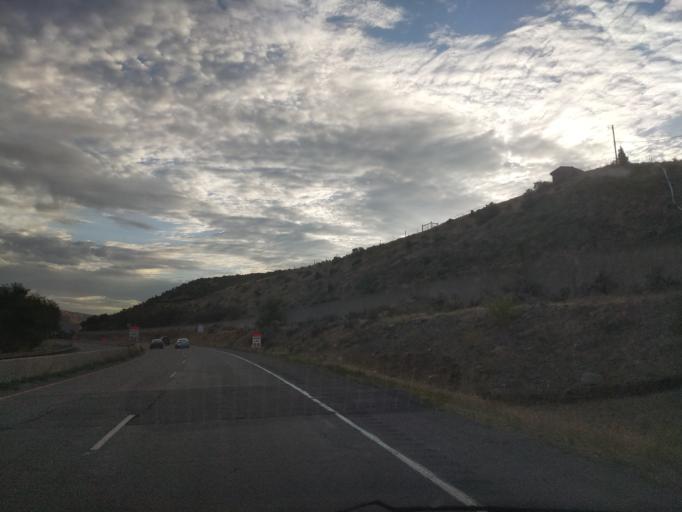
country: US
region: Colorado
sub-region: Mesa County
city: Palisade
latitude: 39.1316
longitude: -108.3236
